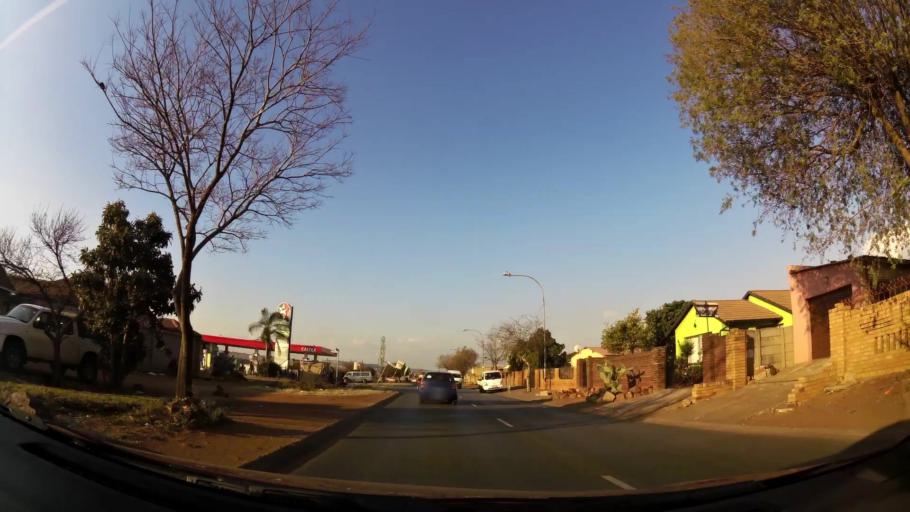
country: ZA
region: Gauteng
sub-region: City of Johannesburg Metropolitan Municipality
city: Soweto
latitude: -26.2276
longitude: 27.8530
